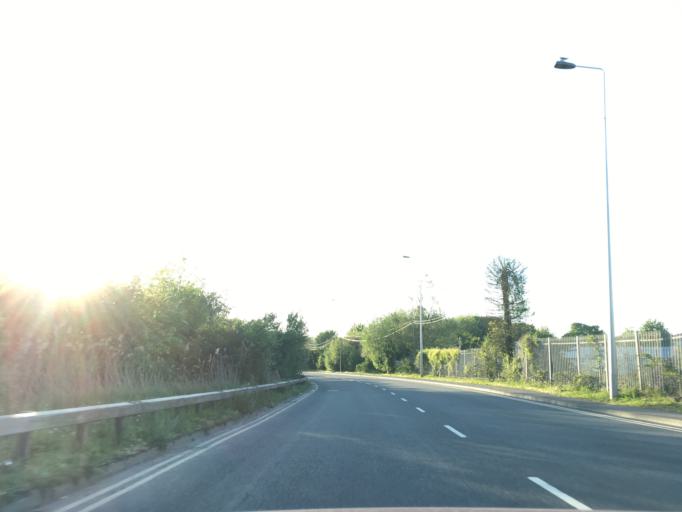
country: GB
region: Wales
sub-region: Newport
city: Newport
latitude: 51.5692
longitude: -2.9974
